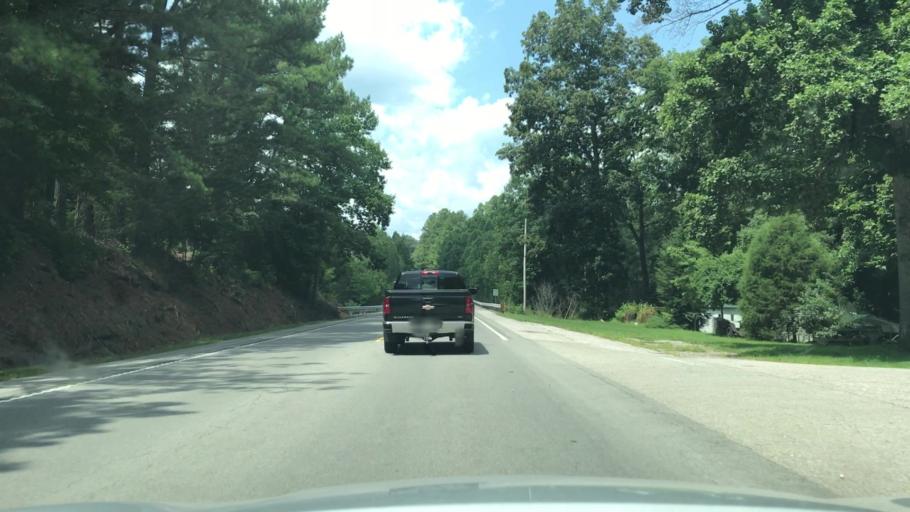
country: US
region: Tennessee
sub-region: Overton County
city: Livingston
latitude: 36.4399
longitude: -85.2607
